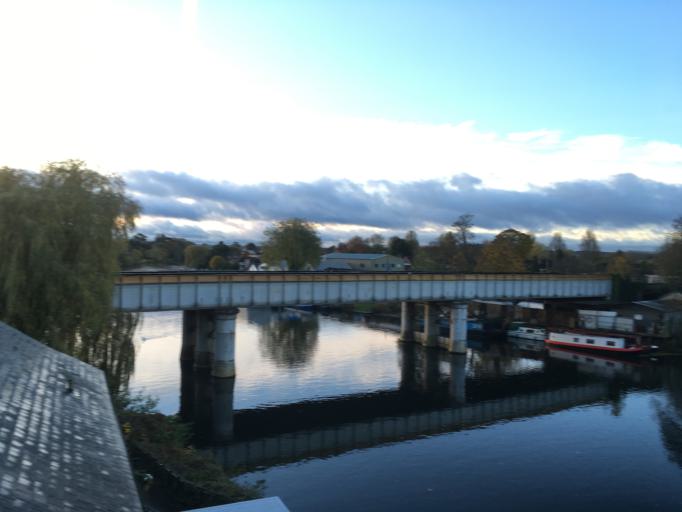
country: GB
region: England
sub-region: Surrey
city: Staines
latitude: 51.4312
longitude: -0.5111
